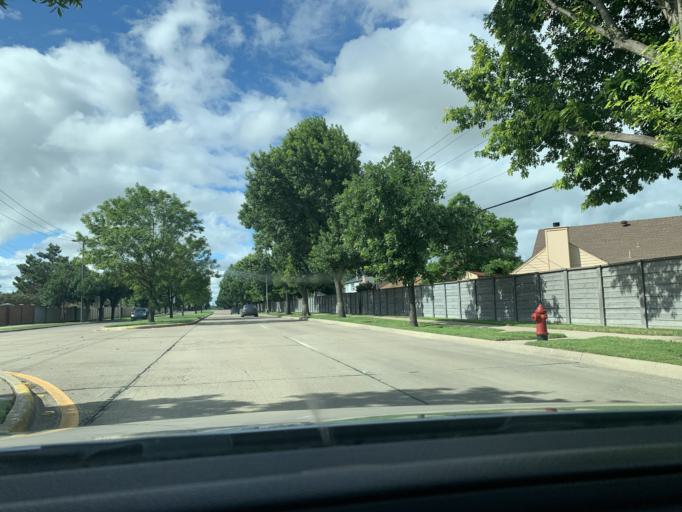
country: US
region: Texas
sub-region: Dallas County
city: Grand Prairie
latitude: 32.6601
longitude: -97.0153
